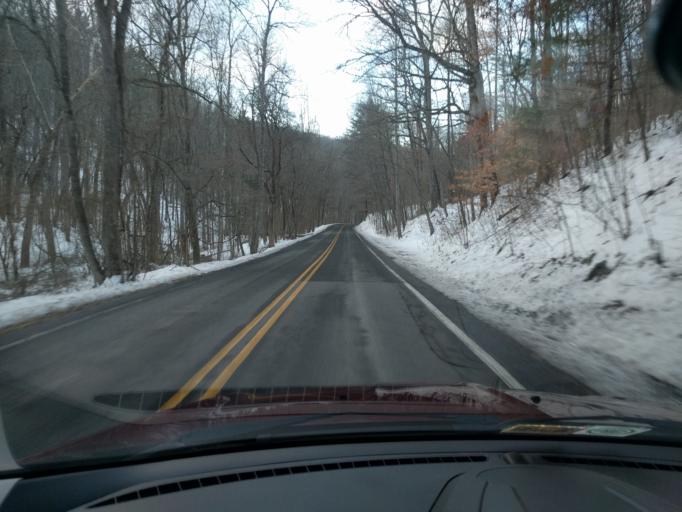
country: US
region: Virginia
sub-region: Bath County
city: Warm Springs
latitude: 38.0878
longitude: -79.8607
